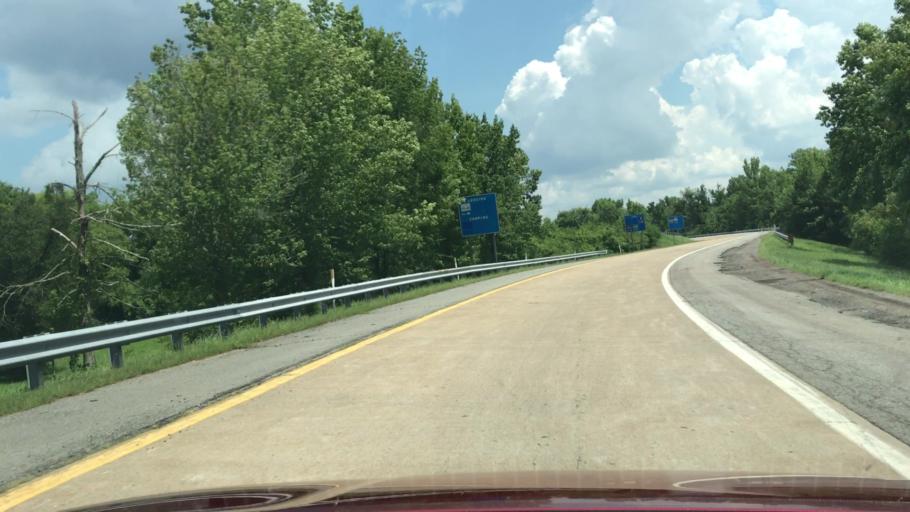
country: US
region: Tennessee
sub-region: Robertson County
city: Ridgetop
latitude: 36.3240
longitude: -86.8714
